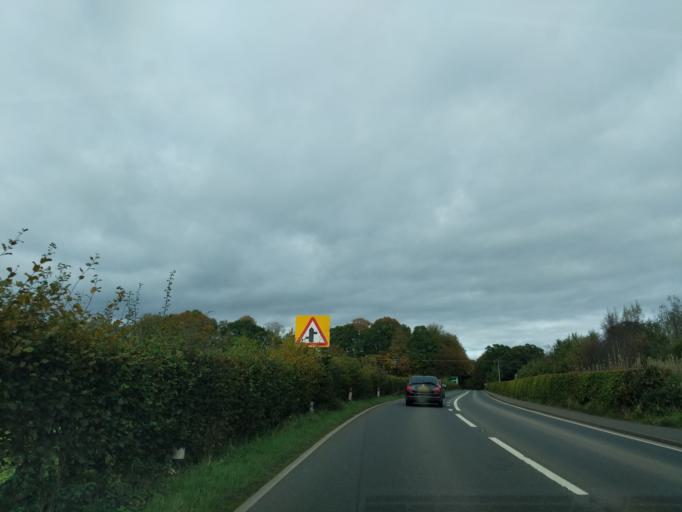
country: GB
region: Scotland
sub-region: Dumfries and Galloway
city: Thornhill
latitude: 55.2479
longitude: -3.7719
